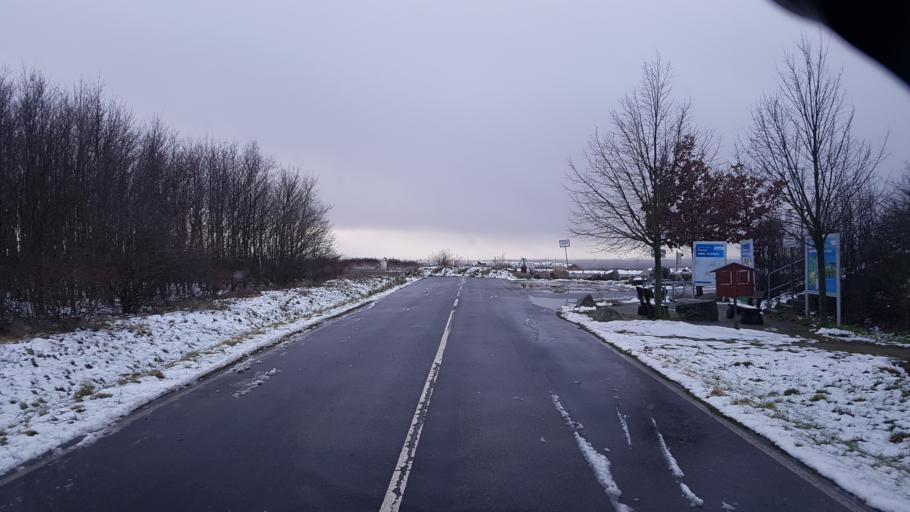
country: DE
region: Brandenburg
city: Heinersbruck
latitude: 51.8462
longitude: 14.5854
